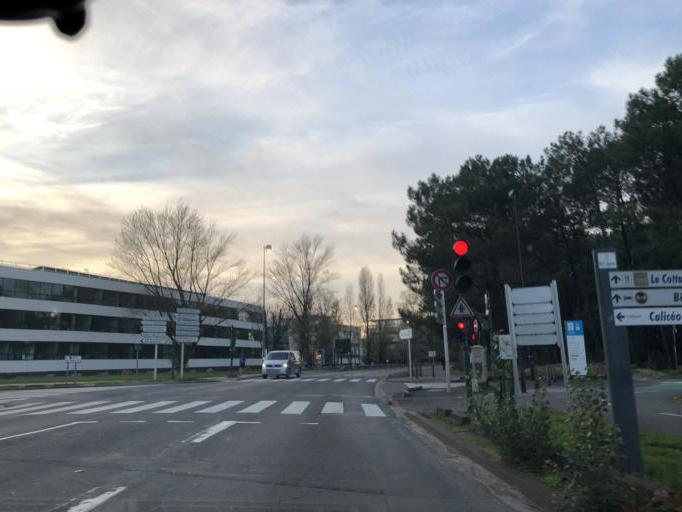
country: FR
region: Aquitaine
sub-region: Departement de la Gironde
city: Le Bouscat
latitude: 44.8772
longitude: -0.5790
